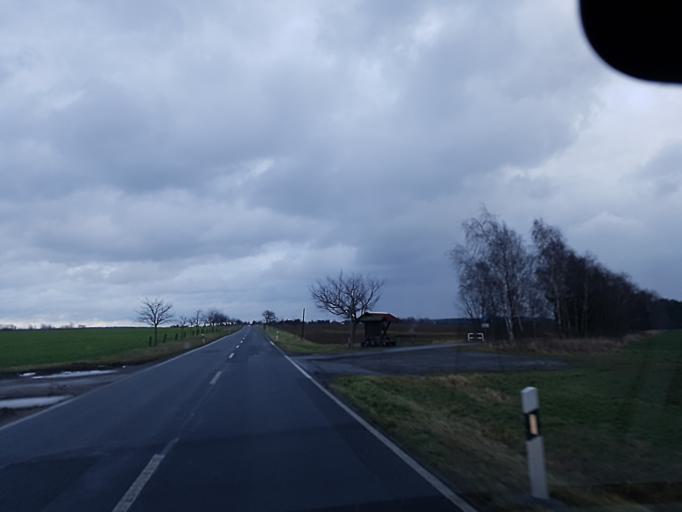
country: DE
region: Brandenburg
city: Ruckersdorf
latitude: 51.5334
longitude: 13.6041
